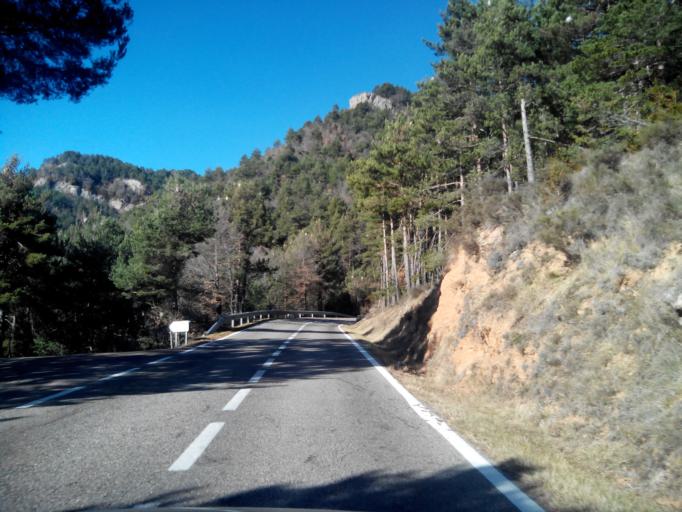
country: ES
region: Catalonia
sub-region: Provincia de Barcelona
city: Capolat
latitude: 42.0914
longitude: 1.7803
